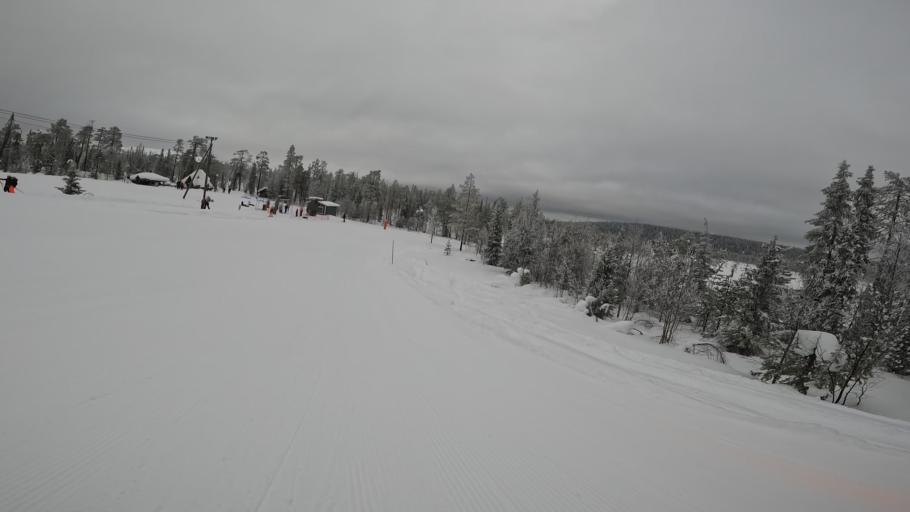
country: FI
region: Lapland
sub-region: Itae-Lappi
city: Salla
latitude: 66.7658
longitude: 28.7991
